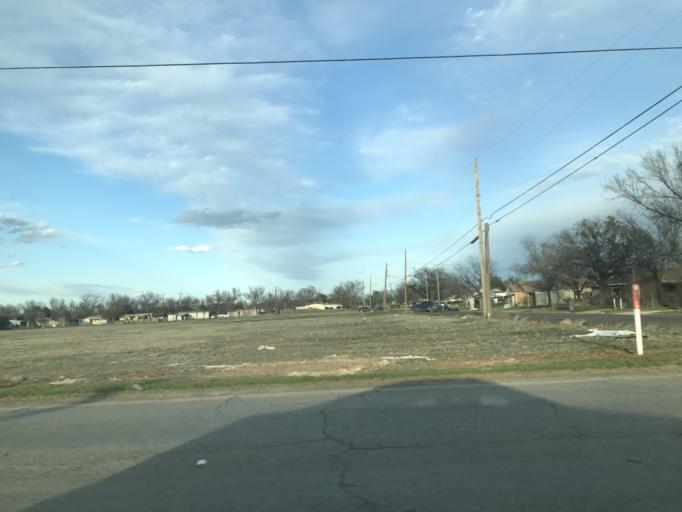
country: US
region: Texas
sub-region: Tom Green County
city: San Angelo
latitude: 31.4929
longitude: -100.4564
